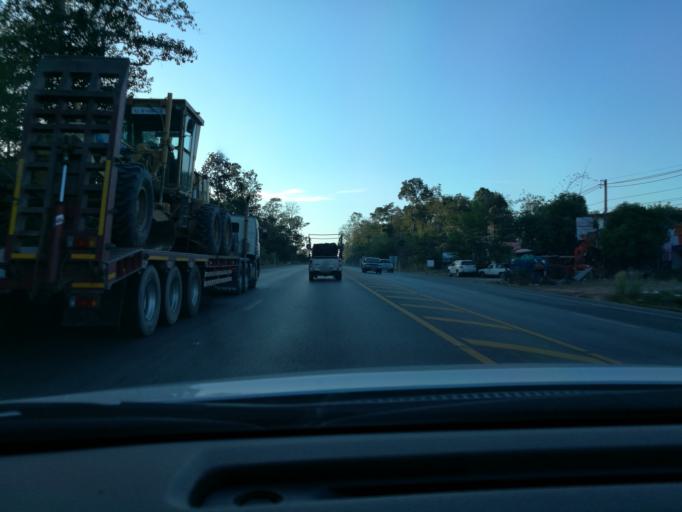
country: TH
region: Phitsanulok
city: Wang Thong
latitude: 16.8449
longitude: 100.5286
